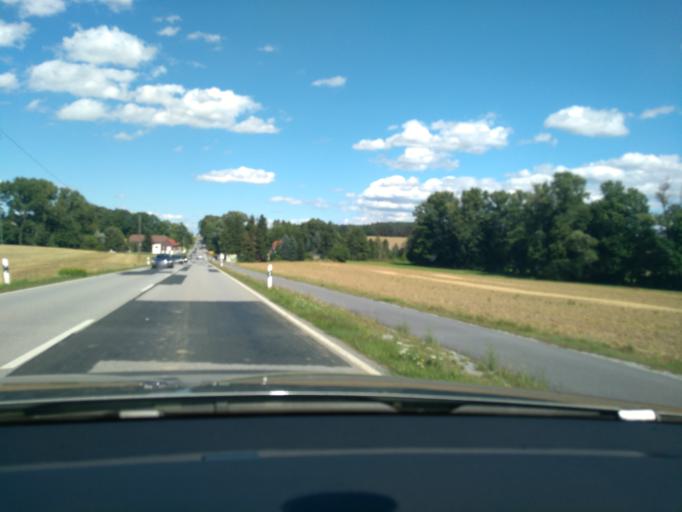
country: DE
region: Saxony
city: Demitz-Thumitz
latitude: 51.1649
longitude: 14.2770
